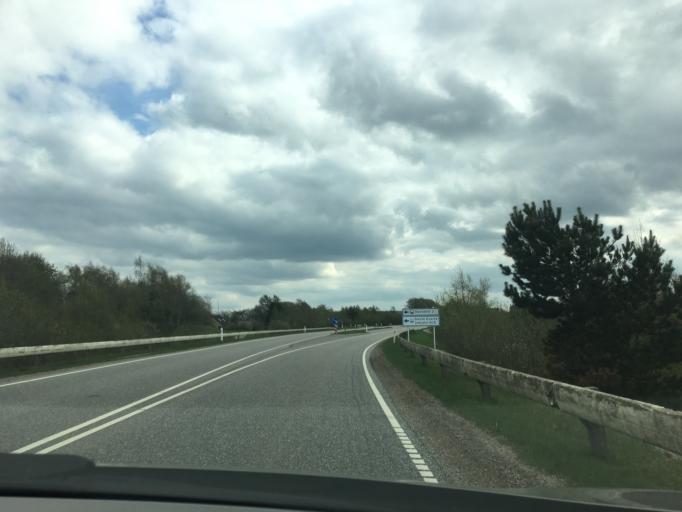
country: DK
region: Central Jutland
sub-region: Horsens Kommune
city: Braedstrup
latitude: 56.0349
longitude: 9.6096
